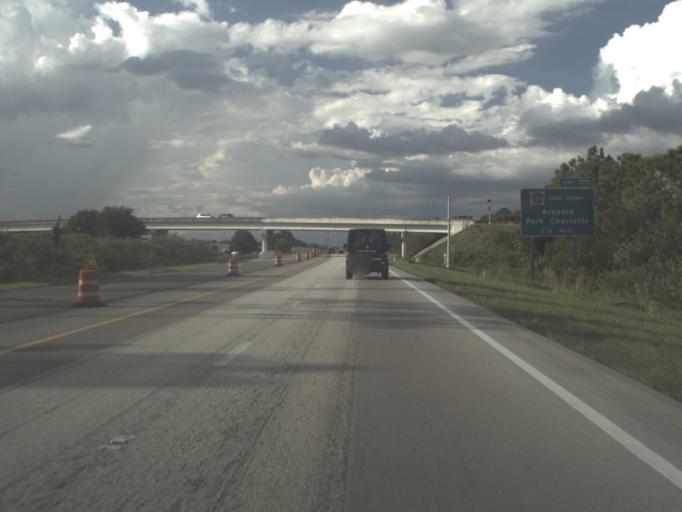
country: US
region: Florida
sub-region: Charlotte County
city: Harbour Heights
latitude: 27.0011
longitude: -82.0361
